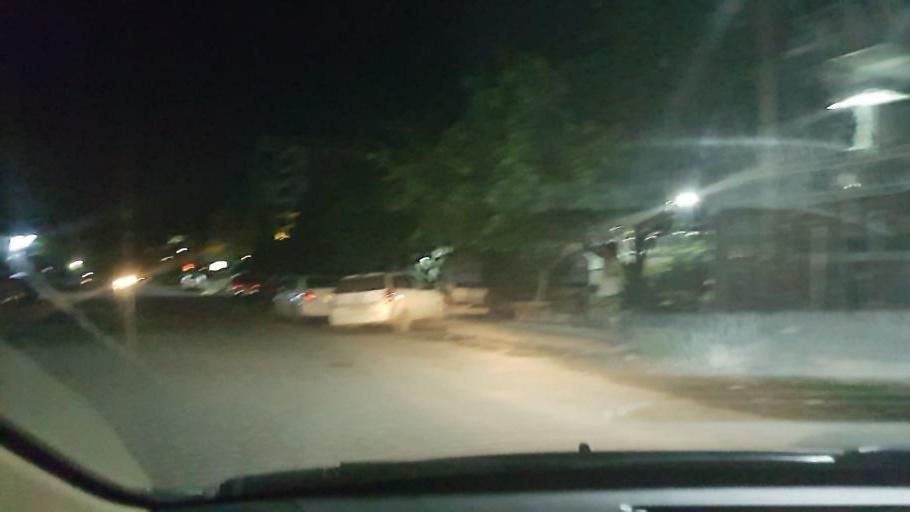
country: MM
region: Mandalay
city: Mandalay
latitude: 21.9811
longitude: 96.0938
